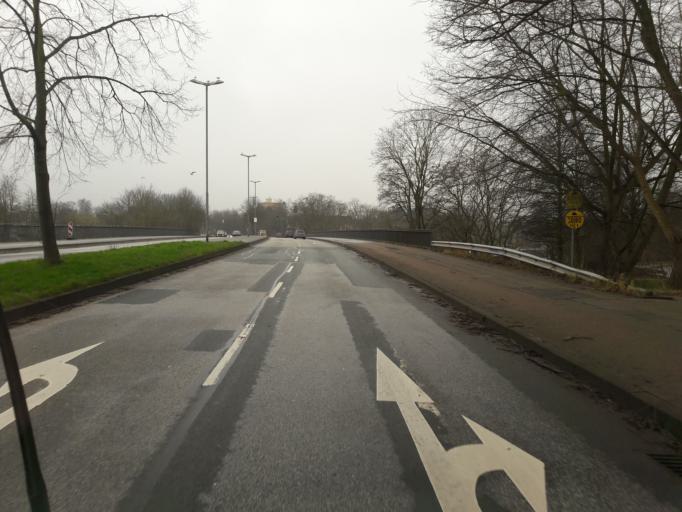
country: DE
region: North Rhine-Westphalia
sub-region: Regierungsbezirk Detmold
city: Minden
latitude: 52.3023
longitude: 8.8952
